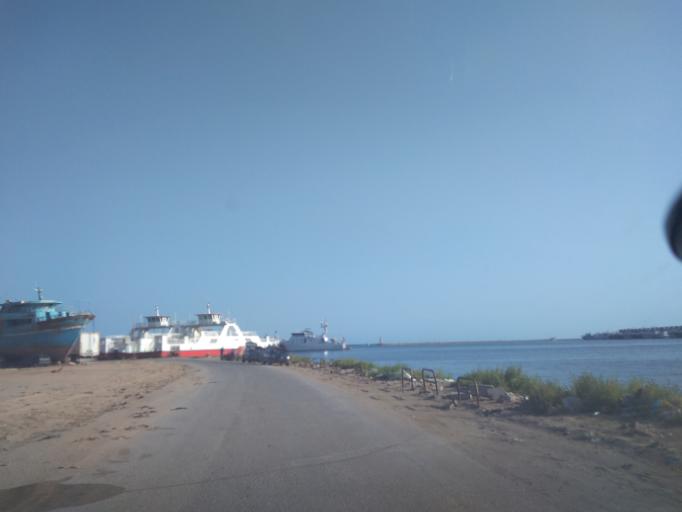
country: TN
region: Safaqis
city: Sfax
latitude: 34.7179
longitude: 10.7675
